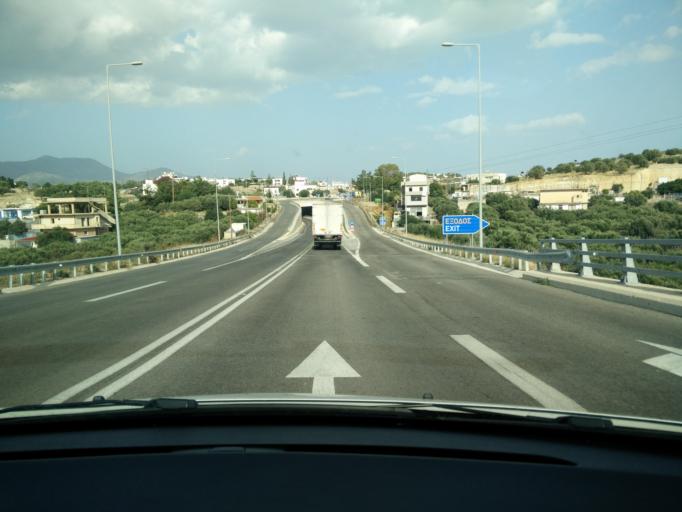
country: GR
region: Crete
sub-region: Nomos Lasithiou
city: Agios Nikolaos
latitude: 35.1825
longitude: 25.7037
